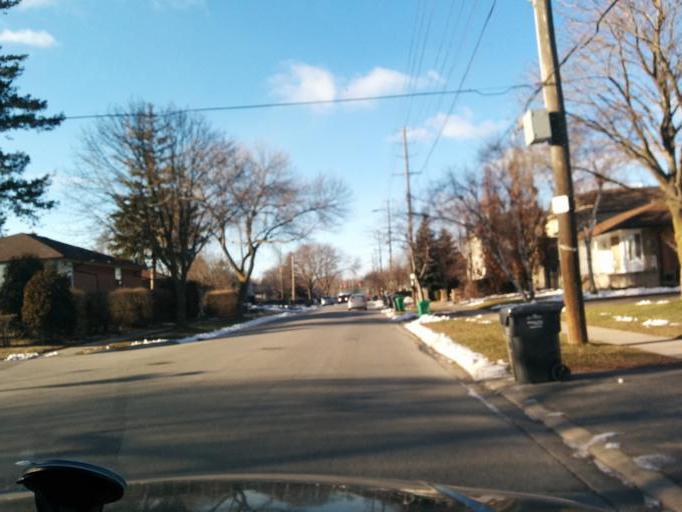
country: CA
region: Ontario
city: Etobicoke
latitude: 43.5878
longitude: -79.5739
